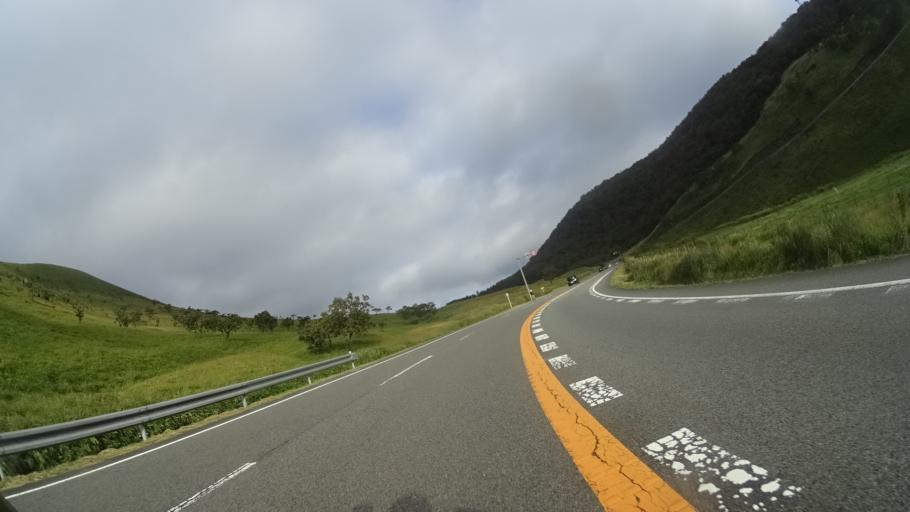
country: JP
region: Oita
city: Beppu
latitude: 33.2630
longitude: 131.3888
